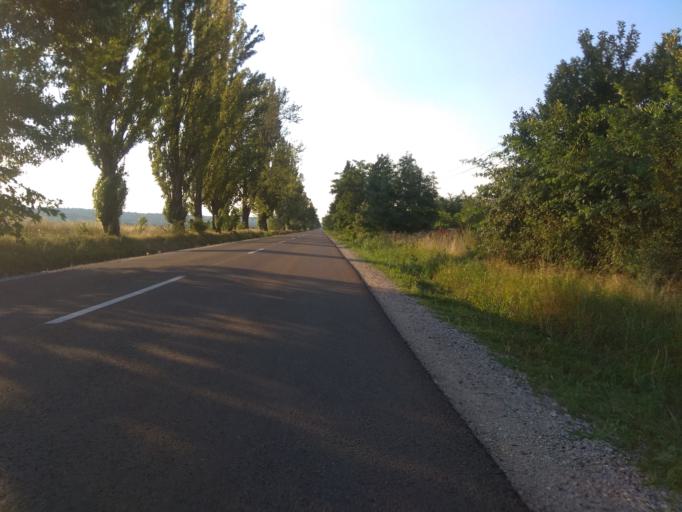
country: HU
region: Borsod-Abauj-Zemplen
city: Nyekladhaza
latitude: 47.9696
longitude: 20.8544
